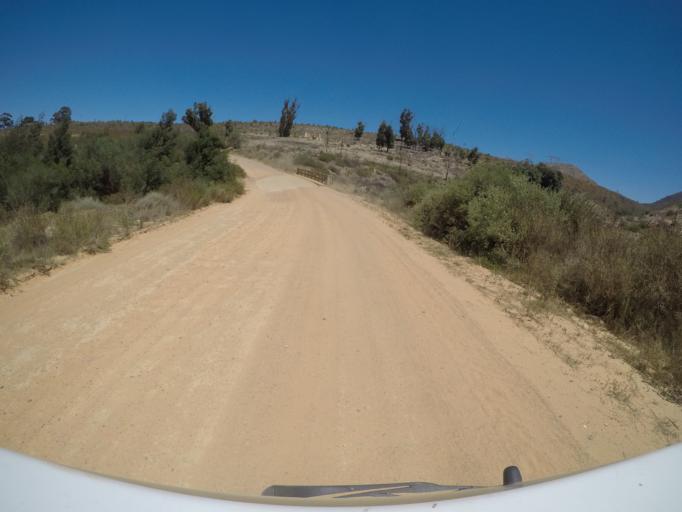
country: ZA
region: Western Cape
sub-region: Overberg District Municipality
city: Grabouw
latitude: -34.2178
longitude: 19.2045
